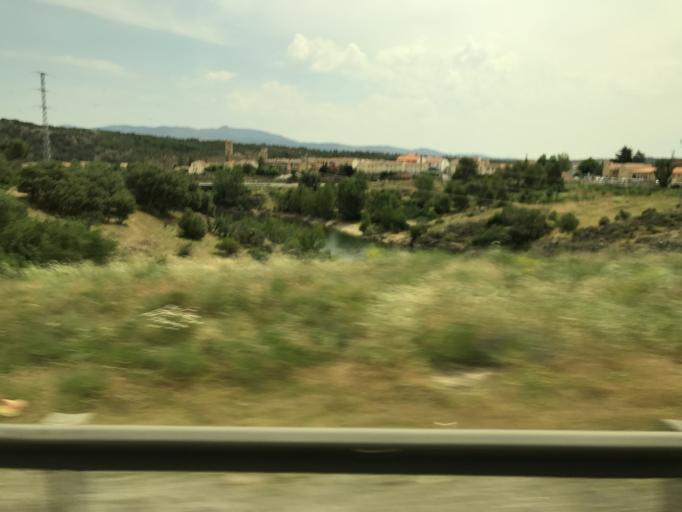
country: ES
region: Madrid
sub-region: Provincia de Madrid
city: Buitrago del Lozoya
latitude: 40.9941
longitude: -3.6419
